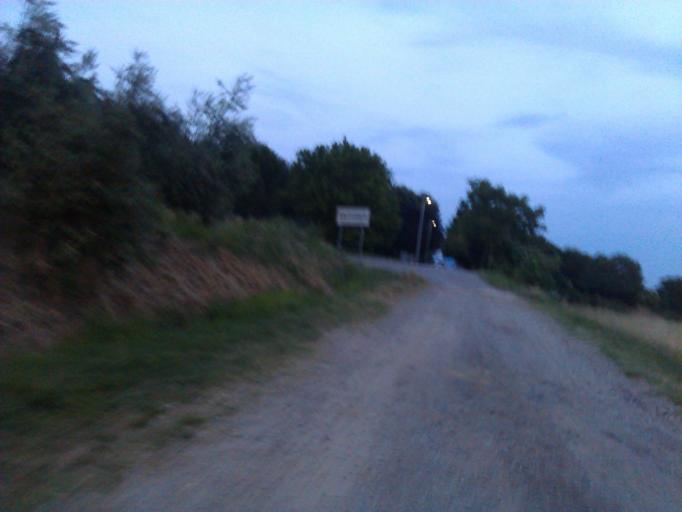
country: IT
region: Tuscany
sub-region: Province of Arezzo
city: Viciomaggio
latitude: 43.4438
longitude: 11.7772
